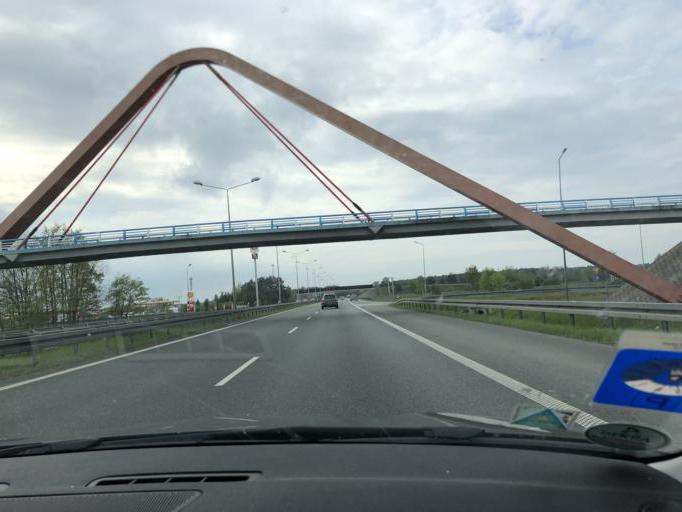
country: PL
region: Opole Voivodeship
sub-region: Powiat opolski
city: Niemodlin
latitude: 50.6771
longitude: 17.6538
